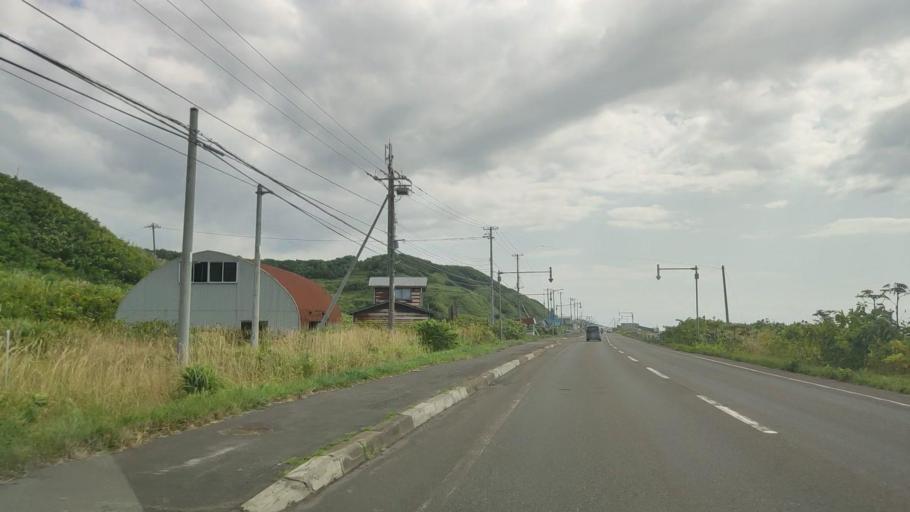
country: JP
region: Hokkaido
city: Rumoi
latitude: 44.1827
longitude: 141.6588
